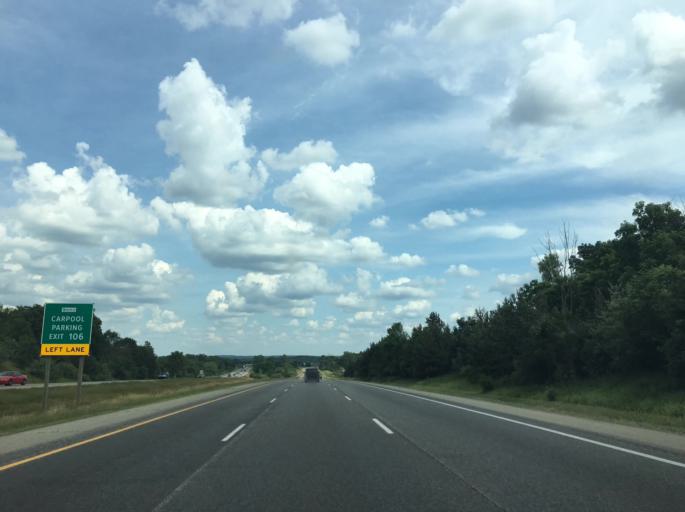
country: US
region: Michigan
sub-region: Genesee County
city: Grand Blanc
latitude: 42.8803
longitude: -83.6115
